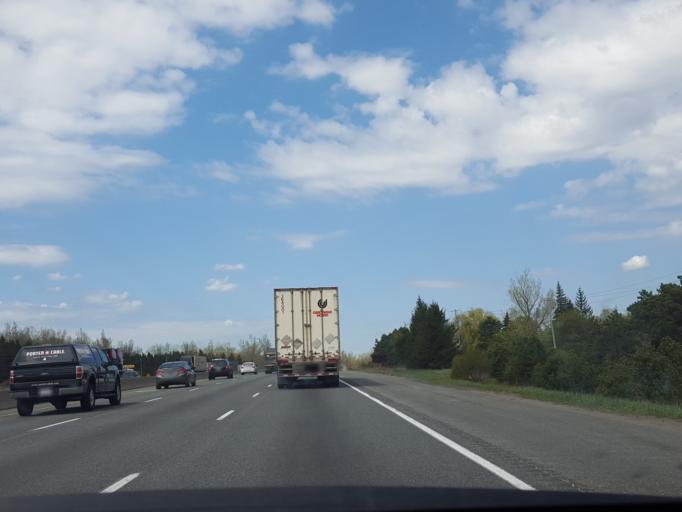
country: CA
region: Ontario
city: Oshawa
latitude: 43.8760
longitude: -78.7863
